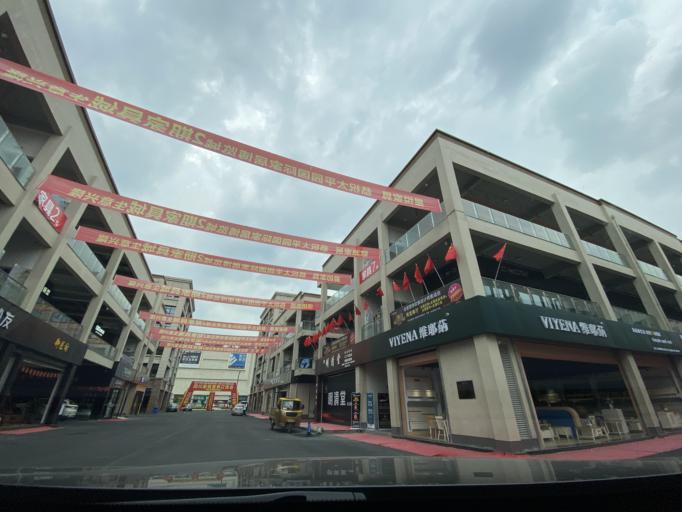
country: CN
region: Sichuan
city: Dongsheng
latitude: 30.6099
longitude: 103.9399
